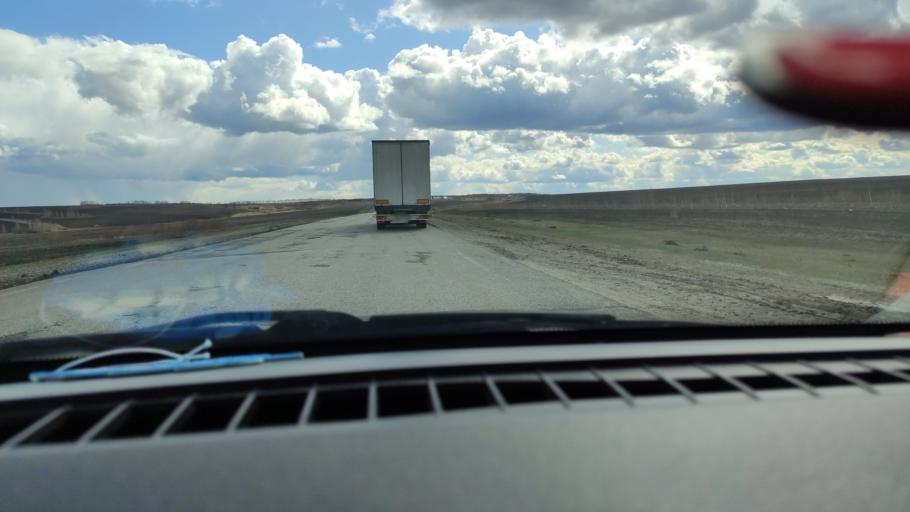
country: RU
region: Samara
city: Varlamovo
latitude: 53.0124
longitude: 48.3326
